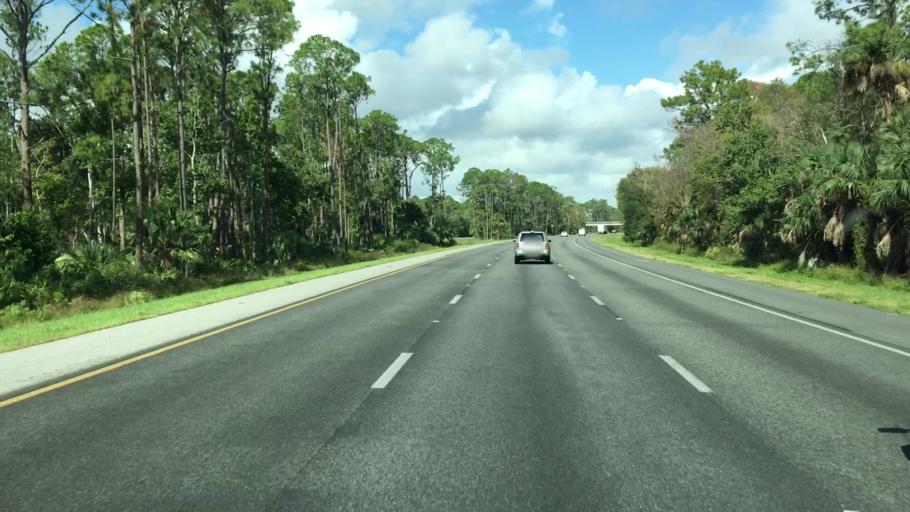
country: US
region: Florida
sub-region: Volusia County
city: Glencoe
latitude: 29.0422
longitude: -81.0059
